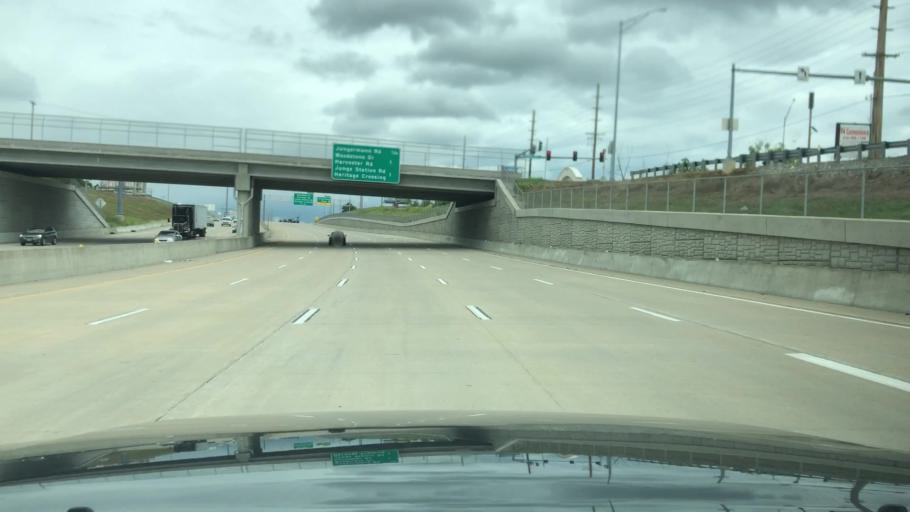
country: US
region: Missouri
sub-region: Saint Charles County
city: Cottleville
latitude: 38.7414
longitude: -90.6092
